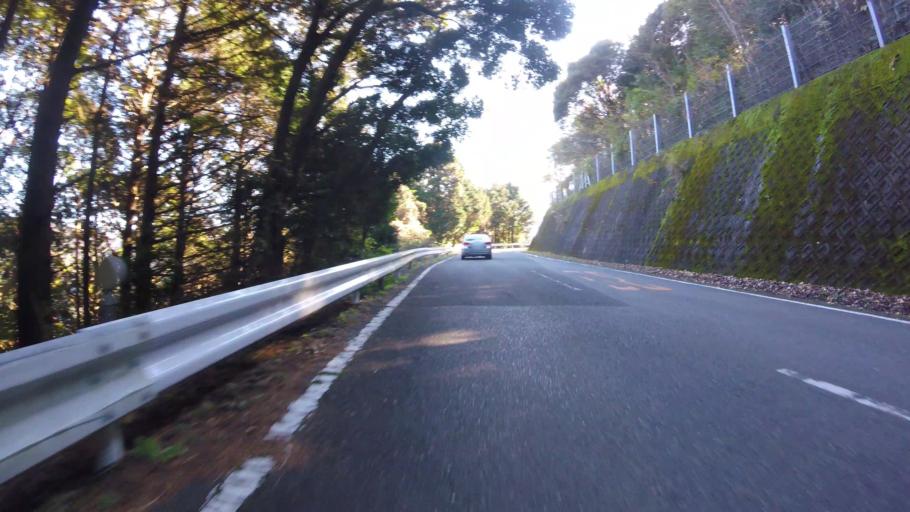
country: JP
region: Shizuoka
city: Shimoda
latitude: 34.7619
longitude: 138.9722
